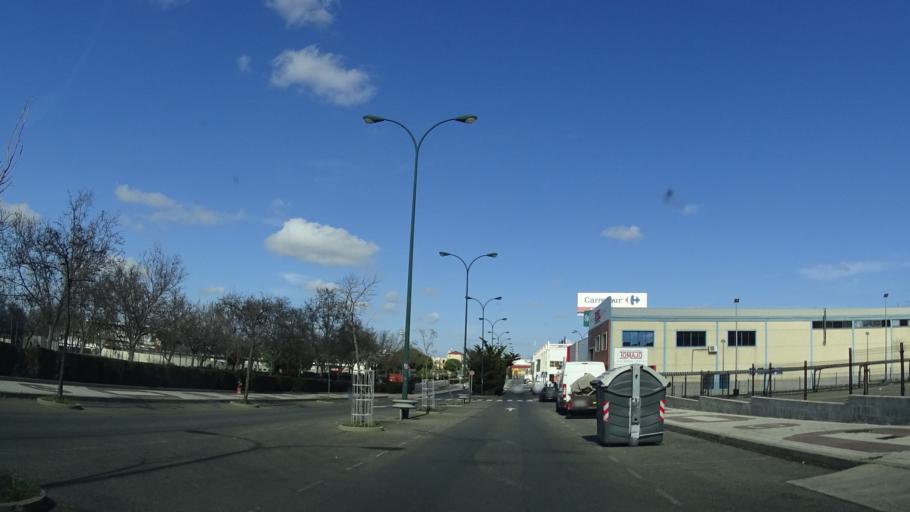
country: ES
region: Castille-La Mancha
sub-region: Provincia de Ciudad Real
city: Puertollano
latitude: 38.7008
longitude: -4.1031
